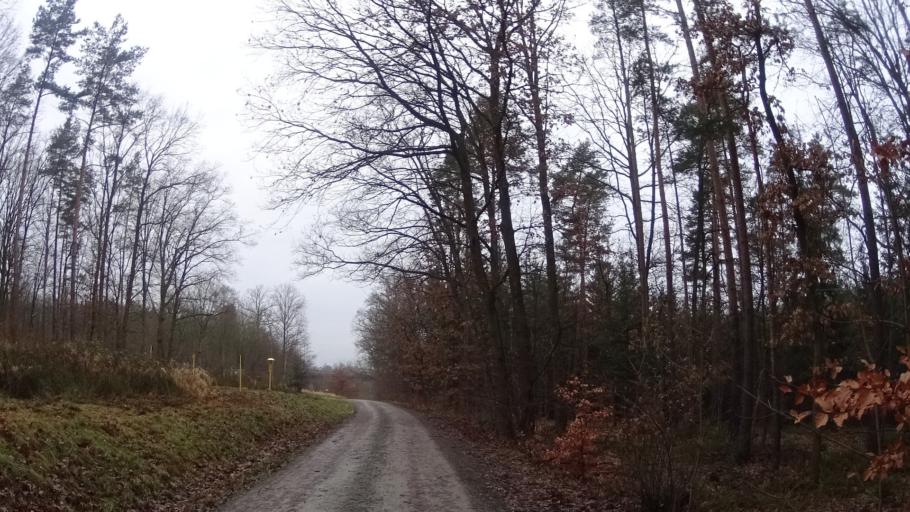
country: DE
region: Thuringia
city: Ruttersdorf-Lotschen
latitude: 50.8692
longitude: 11.7403
